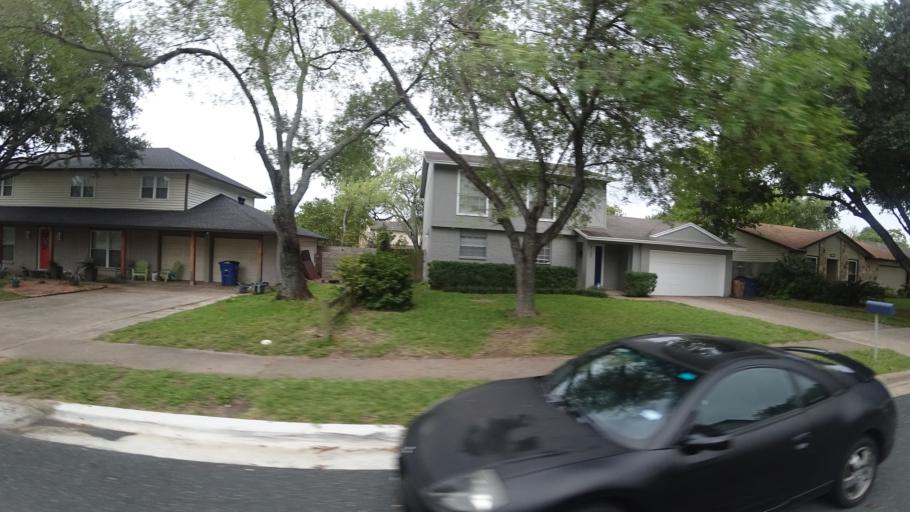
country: US
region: Texas
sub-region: Travis County
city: Austin
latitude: 30.3428
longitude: -97.6902
